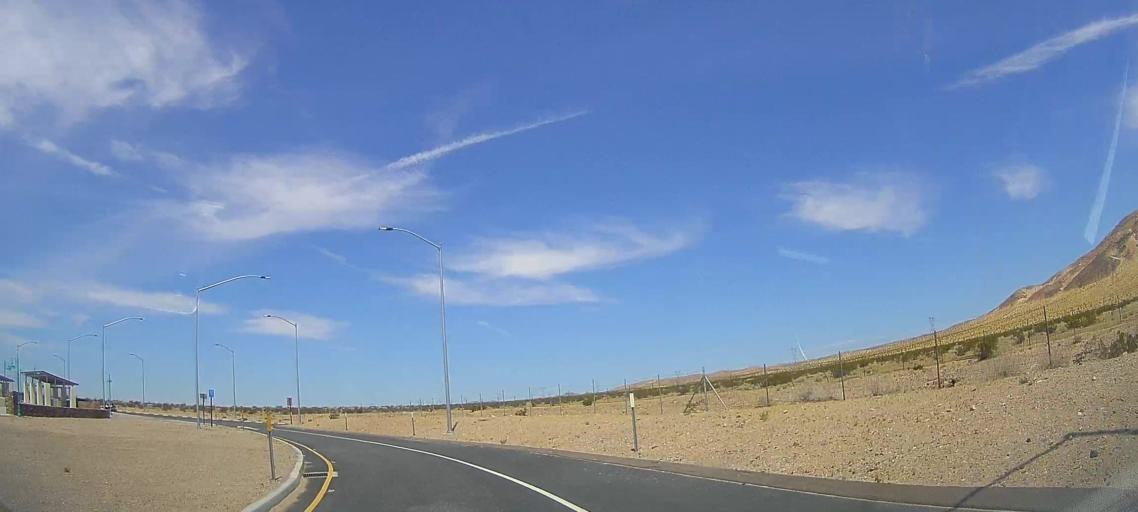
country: US
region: California
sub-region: San Bernardino County
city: Fort Irwin
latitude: 35.0350
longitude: -116.4695
